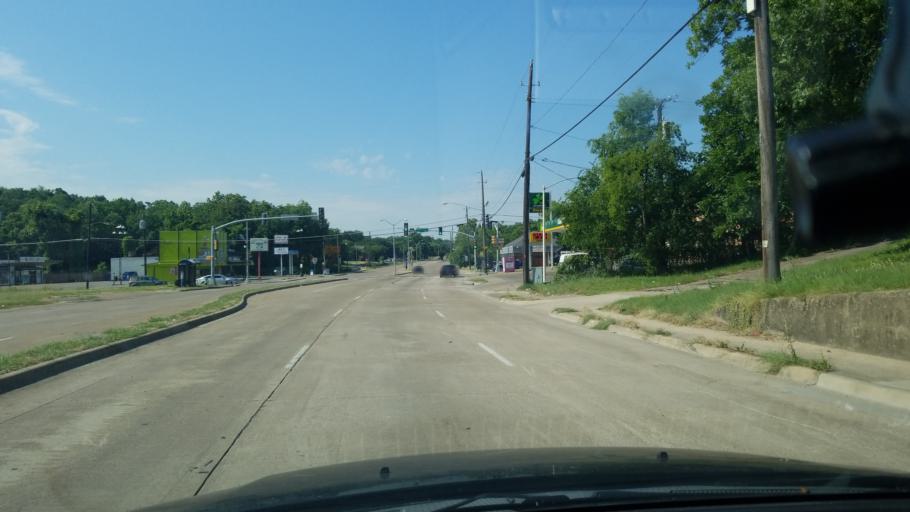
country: US
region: Texas
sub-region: Dallas County
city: Dallas
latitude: 32.7399
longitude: -96.7985
